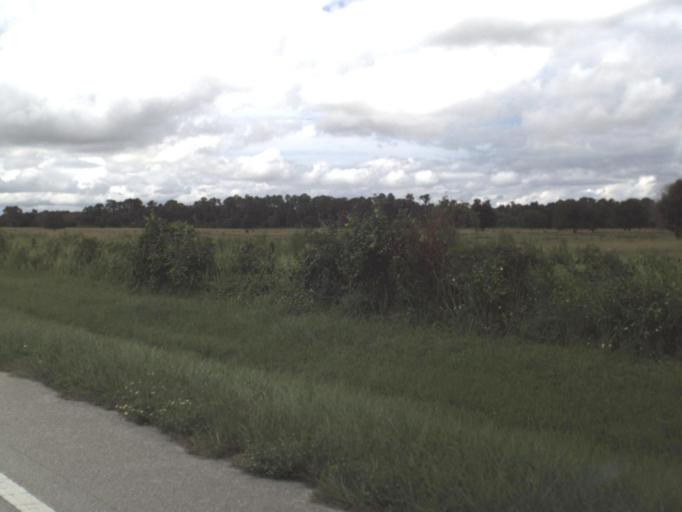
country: US
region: Florida
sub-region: Hardee County
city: Bowling Green
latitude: 27.5949
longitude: -81.9905
